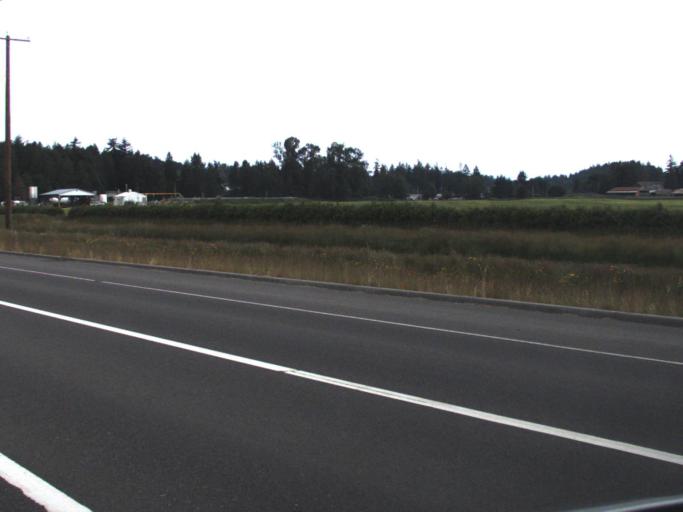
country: US
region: Washington
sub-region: Whatcom County
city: Lynden
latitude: 48.9974
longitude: -122.4851
